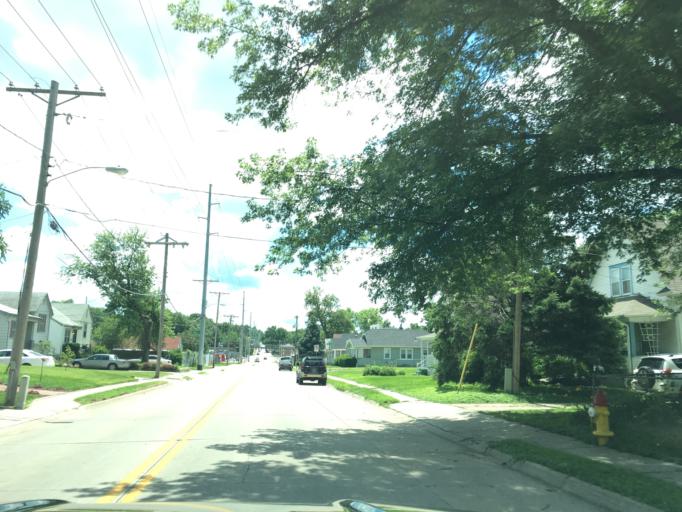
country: US
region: Nebraska
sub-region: Douglas County
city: Omaha
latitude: 41.2487
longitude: -95.9902
